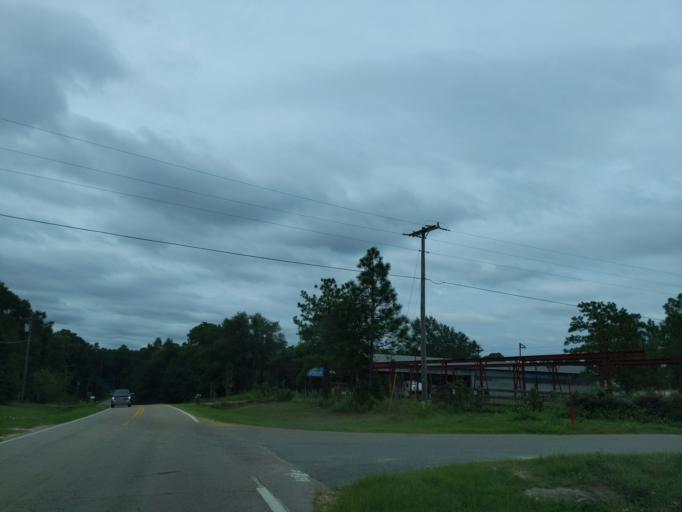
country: US
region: Florida
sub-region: Gadsden County
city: Midway
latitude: 30.4376
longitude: -84.4117
